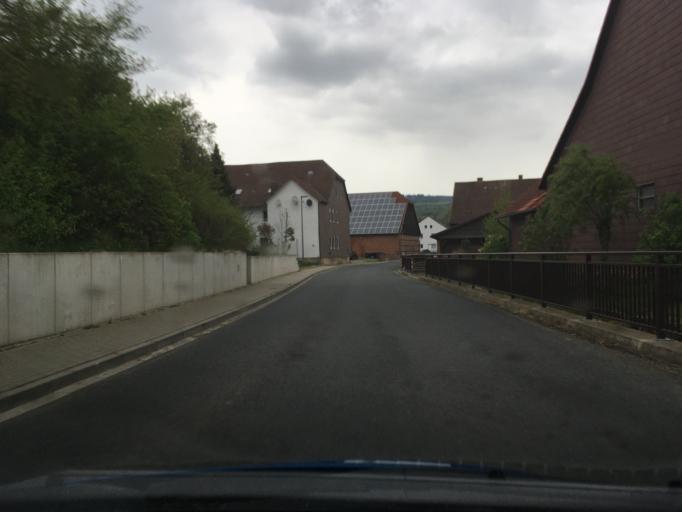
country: DE
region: Lower Saxony
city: Eimen
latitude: 51.8684
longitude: 9.8104
